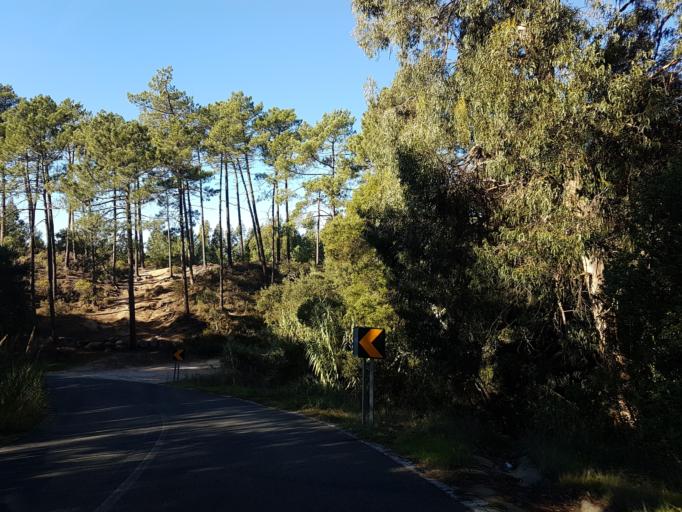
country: PT
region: Lisbon
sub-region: Cascais
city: Alcabideche
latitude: 38.7600
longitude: -9.4118
